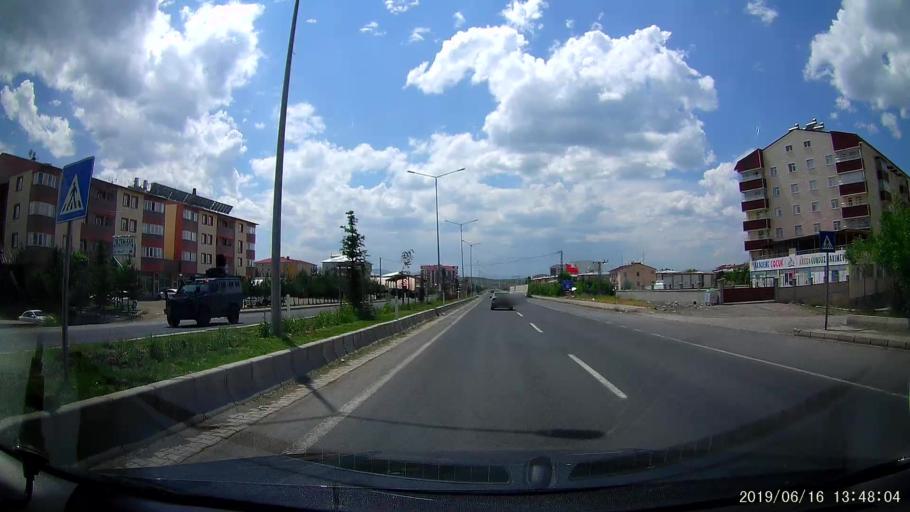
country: TR
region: Agri
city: Agri
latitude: 39.7144
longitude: 43.0141
